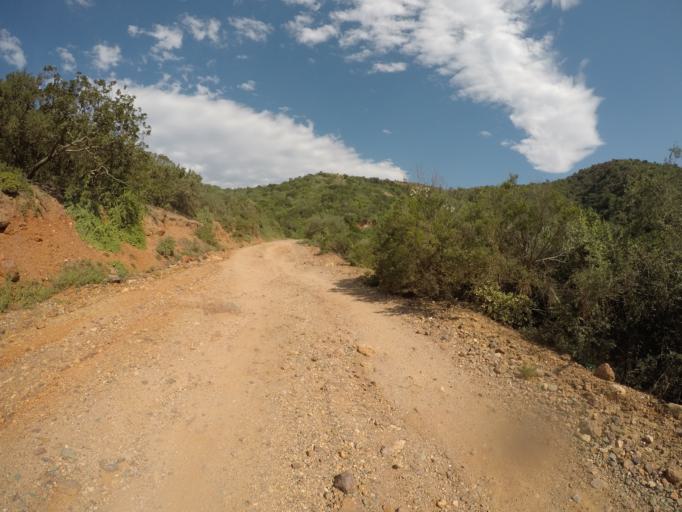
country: ZA
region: Eastern Cape
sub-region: Cacadu District Municipality
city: Kareedouw
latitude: -33.6570
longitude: 24.4276
